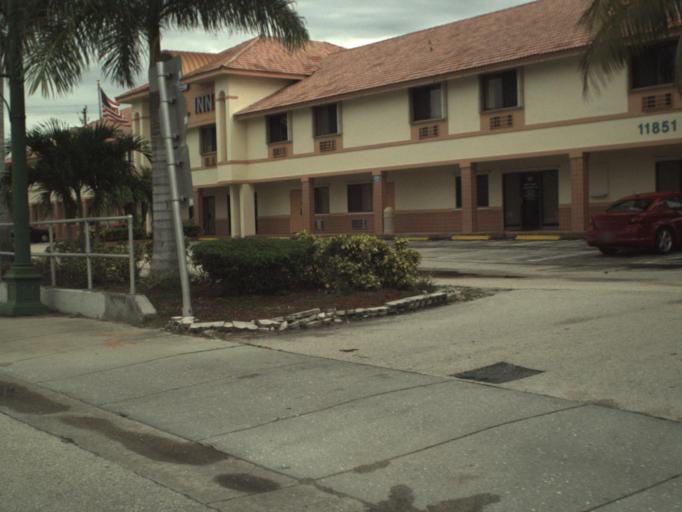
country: US
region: Florida
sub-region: Palm Beach County
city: Wellington
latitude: 26.6814
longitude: -80.2317
